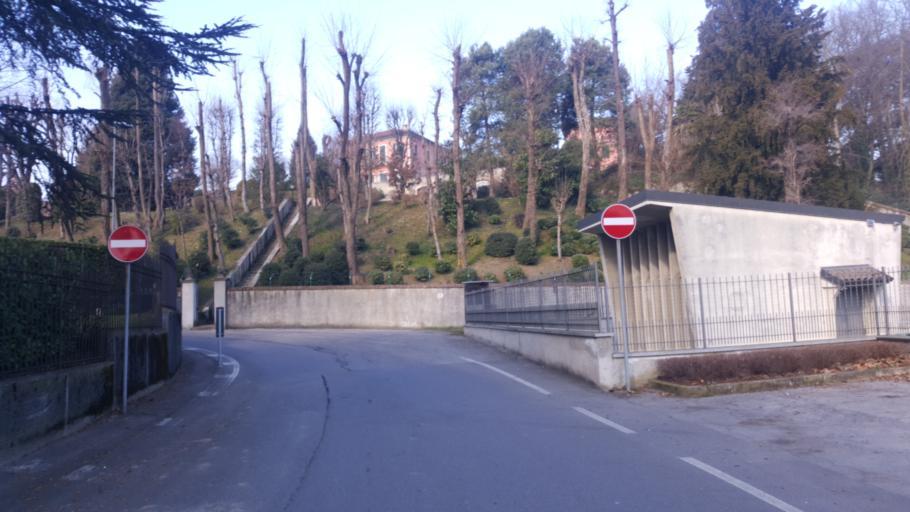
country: IT
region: Lombardy
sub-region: Provincia di Monza e Brianza
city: Lentate sul Seveso
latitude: 45.6792
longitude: 9.1248
